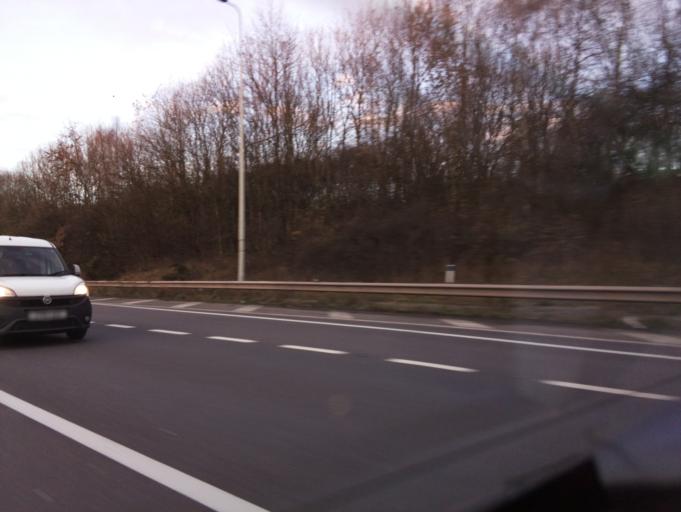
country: GB
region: England
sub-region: Staffordshire
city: Essington
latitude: 52.6257
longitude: -2.0428
